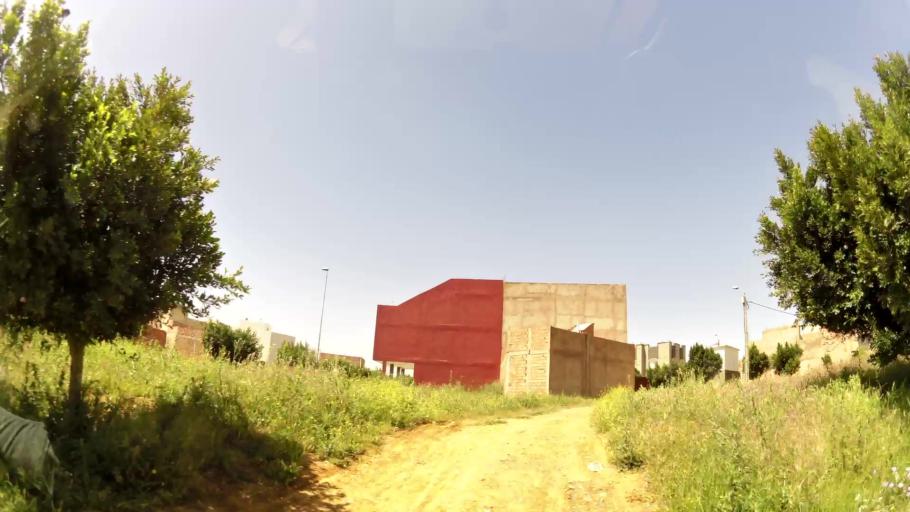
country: MA
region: Rabat-Sale-Zemmour-Zaer
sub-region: Khemisset
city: Khemisset
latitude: 33.8102
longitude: -6.0865
